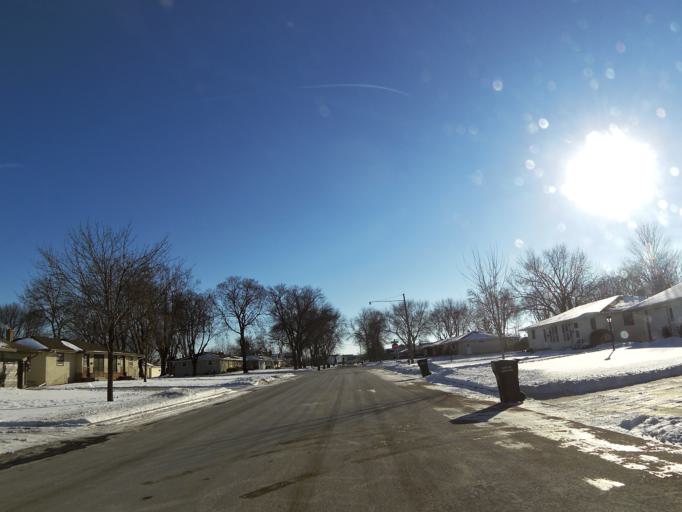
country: US
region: Minnesota
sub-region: Scott County
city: Shakopee
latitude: 44.7890
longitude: -93.5278
